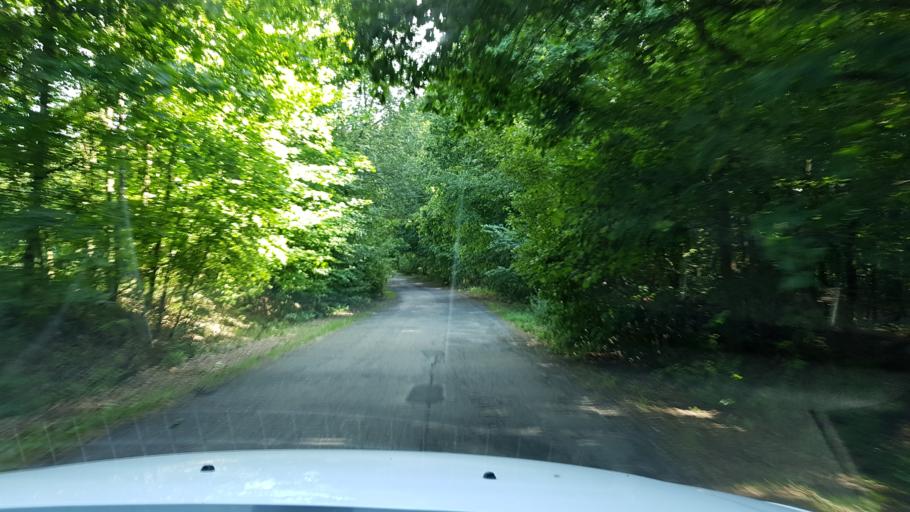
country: PL
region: West Pomeranian Voivodeship
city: Trzcinsko Zdroj
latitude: 52.9411
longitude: 14.5523
